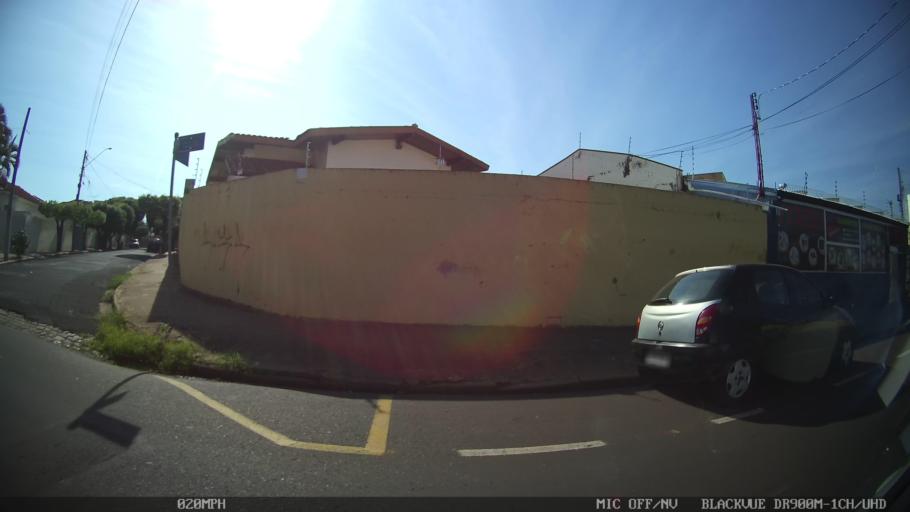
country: BR
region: Sao Paulo
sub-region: Sao Jose Do Rio Preto
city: Sao Jose do Rio Preto
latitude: -20.8078
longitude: -49.3930
